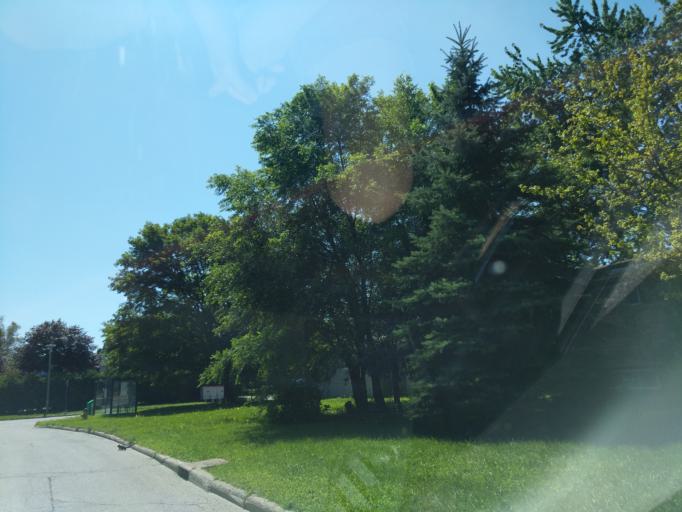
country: CA
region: Ontario
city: Bells Corners
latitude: 45.3483
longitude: -75.8351
